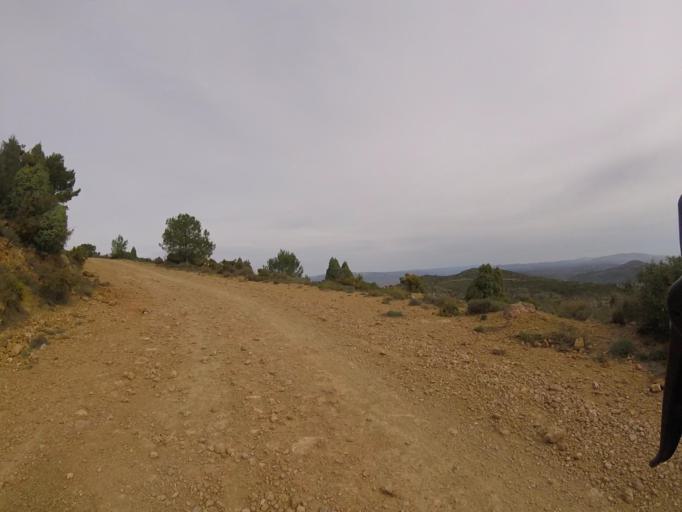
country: ES
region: Valencia
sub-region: Provincia de Castello
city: Benicassim
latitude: 40.0867
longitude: 0.0384
